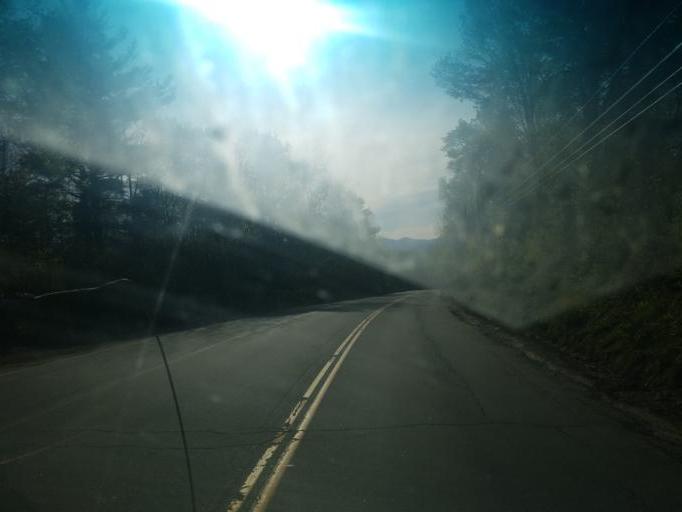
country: US
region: New Hampshire
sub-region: Grafton County
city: Deerfield
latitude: 44.2820
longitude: -71.6535
